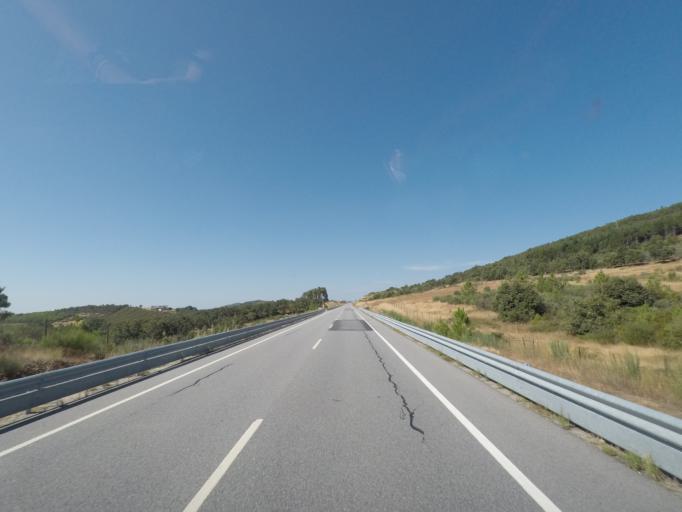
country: PT
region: Braganca
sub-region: Mogadouro
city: Mogadouro
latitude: 41.3468
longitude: -6.6175
